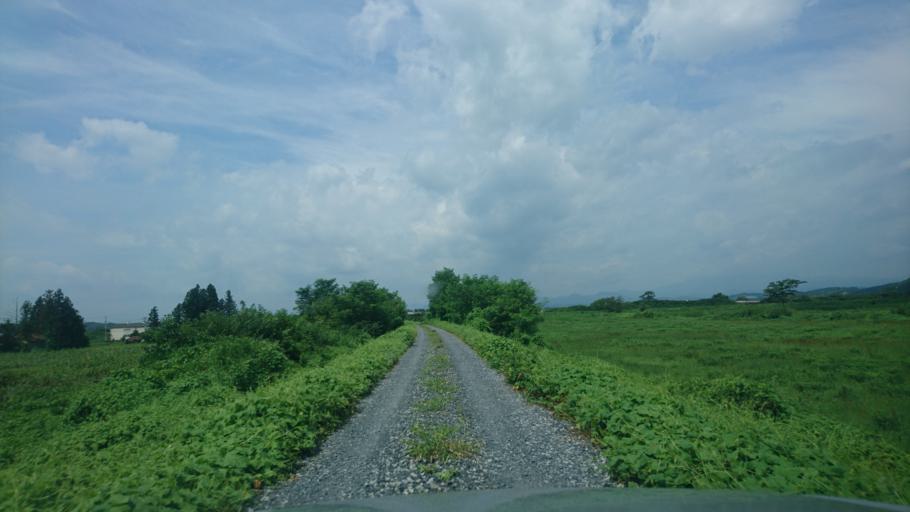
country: JP
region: Iwate
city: Ichinoseki
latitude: 38.7741
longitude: 141.0477
